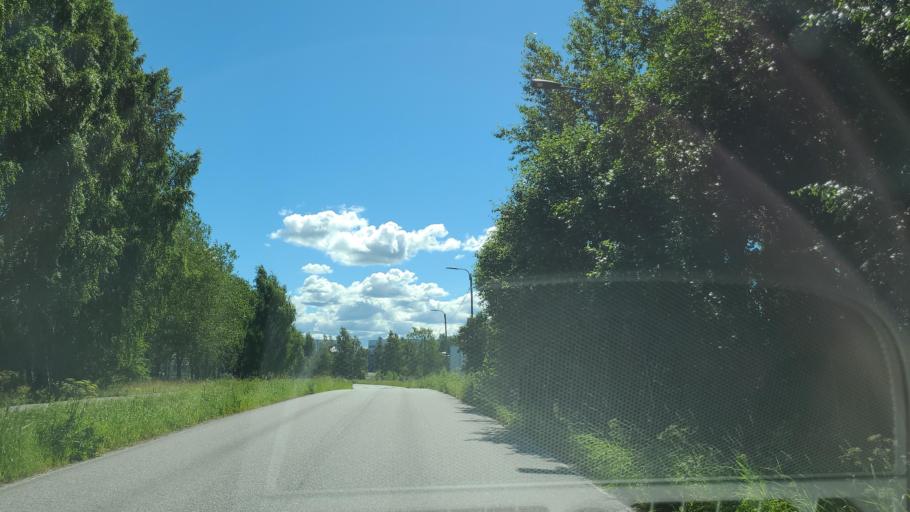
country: FI
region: Ostrobothnia
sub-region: Vaasa
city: Ristinummi
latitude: 63.0620
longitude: 21.7267
